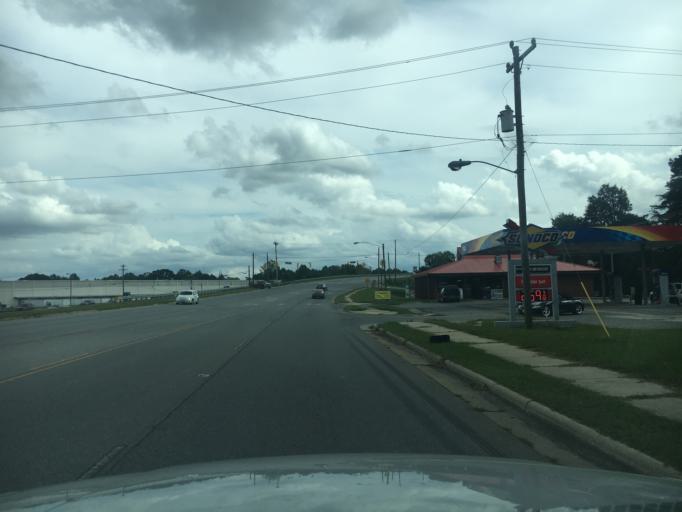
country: US
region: North Carolina
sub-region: Gaston County
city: Bessemer City
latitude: 35.2867
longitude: -81.2414
